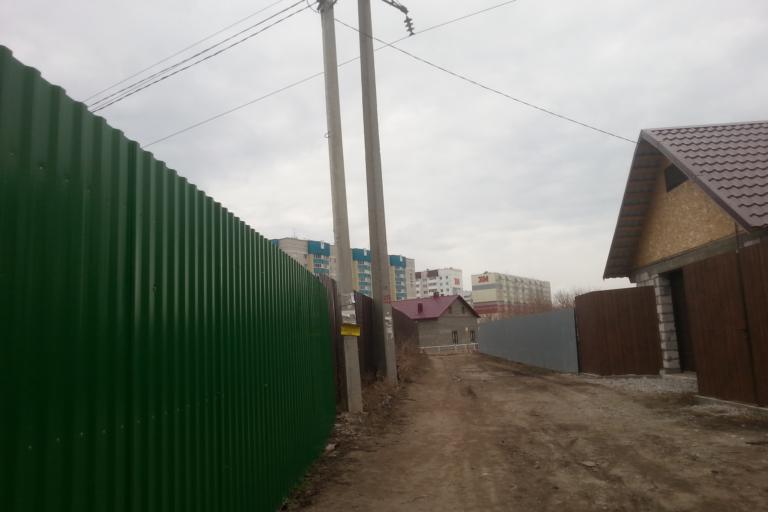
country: RU
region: Altai Krai
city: Novosilikatnyy
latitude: 53.3241
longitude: 83.6838
